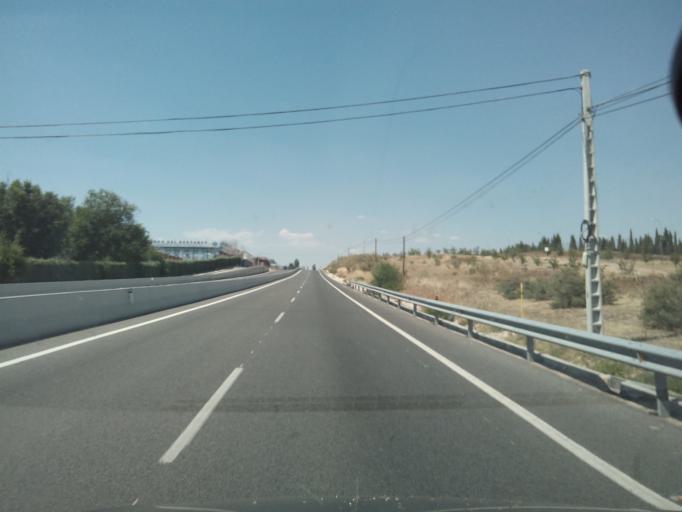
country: ES
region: Madrid
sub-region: Provincia de Madrid
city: Ajalvir
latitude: 40.4976
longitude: -3.4790
